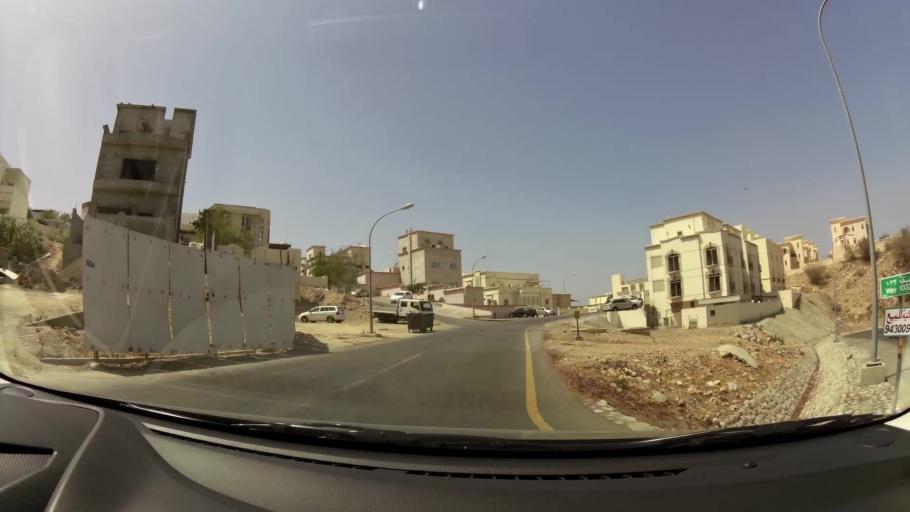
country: OM
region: Muhafazat Masqat
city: Muscat
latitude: 23.6173
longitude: 58.5079
